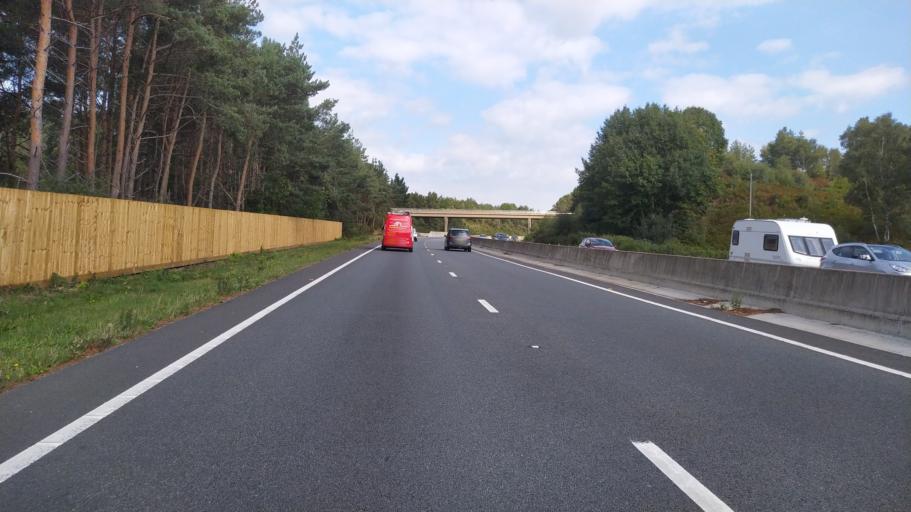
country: GB
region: England
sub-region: Hampshire
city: Ringwood
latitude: 50.8165
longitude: -1.8140
